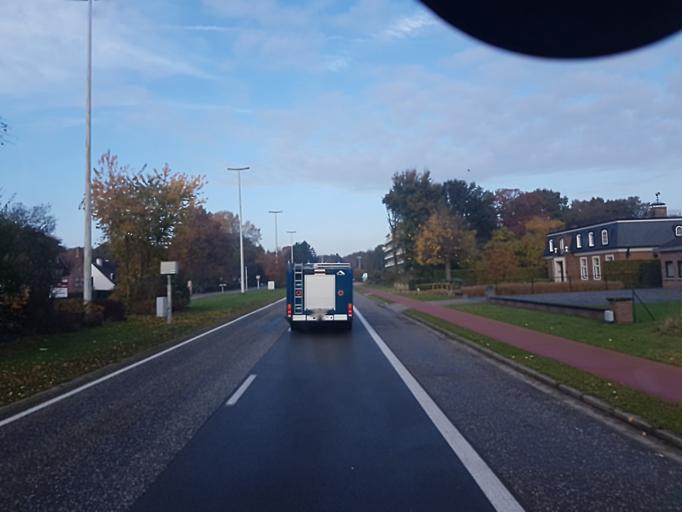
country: BE
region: Flanders
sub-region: Provincie Antwerpen
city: Turnhout
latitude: 51.3149
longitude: 4.9237
